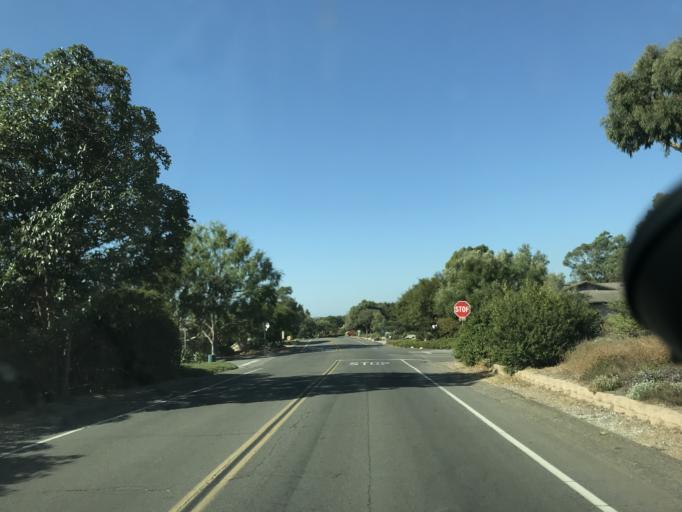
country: US
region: California
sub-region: Santa Barbara County
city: Goleta
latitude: 34.4563
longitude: -119.7882
